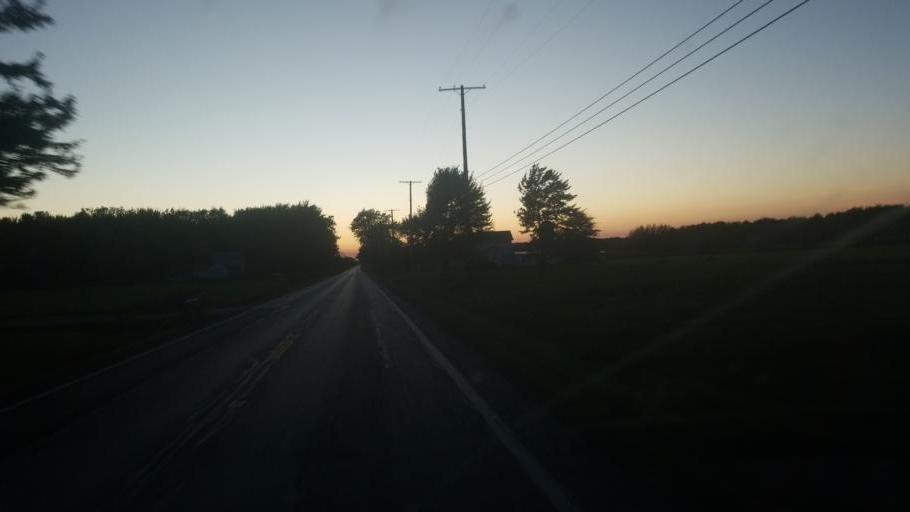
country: US
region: Ohio
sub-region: Ashtabula County
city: Jefferson
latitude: 41.7515
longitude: -80.6771
